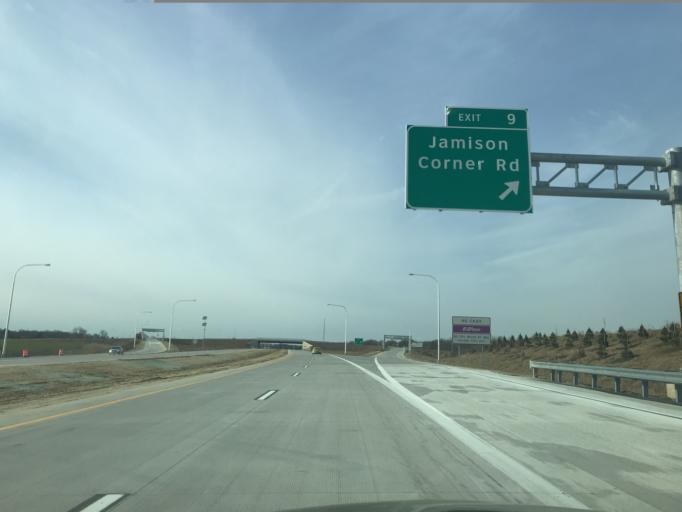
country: US
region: Delaware
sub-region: New Castle County
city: Middletown
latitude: 39.5250
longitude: -75.6734
